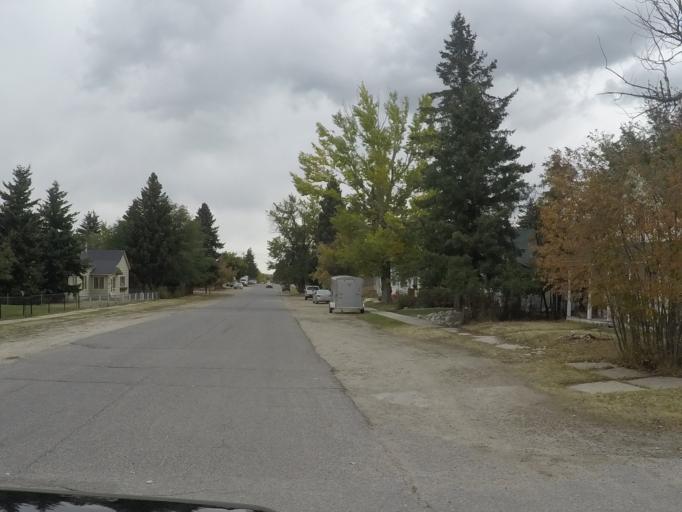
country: US
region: Montana
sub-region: Carbon County
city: Red Lodge
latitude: 45.1899
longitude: -109.2445
